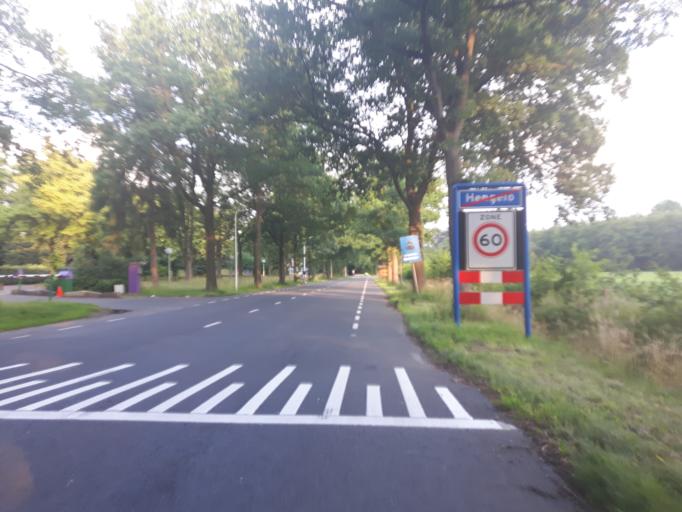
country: NL
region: Overijssel
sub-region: Gemeente Hengelo
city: Hengelo
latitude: 52.2438
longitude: 6.8083
